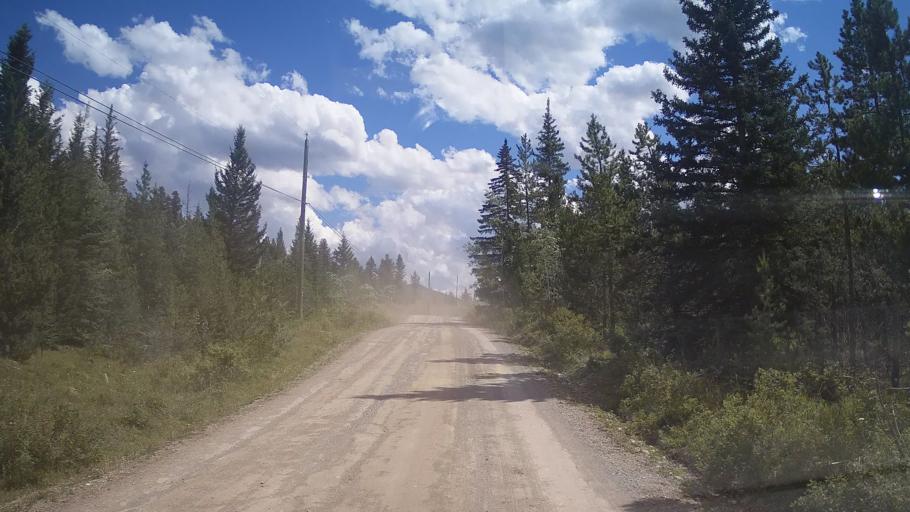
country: CA
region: British Columbia
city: Lillooet
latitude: 51.2910
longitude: -121.9765
